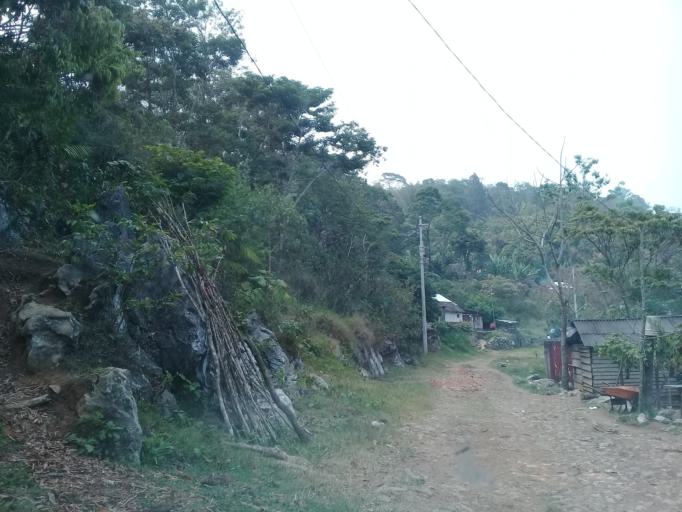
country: MX
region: Veracruz
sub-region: Tezonapa
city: Laguna Chica (Pueblo Nuevo)
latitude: 18.5895
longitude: -96.7470
